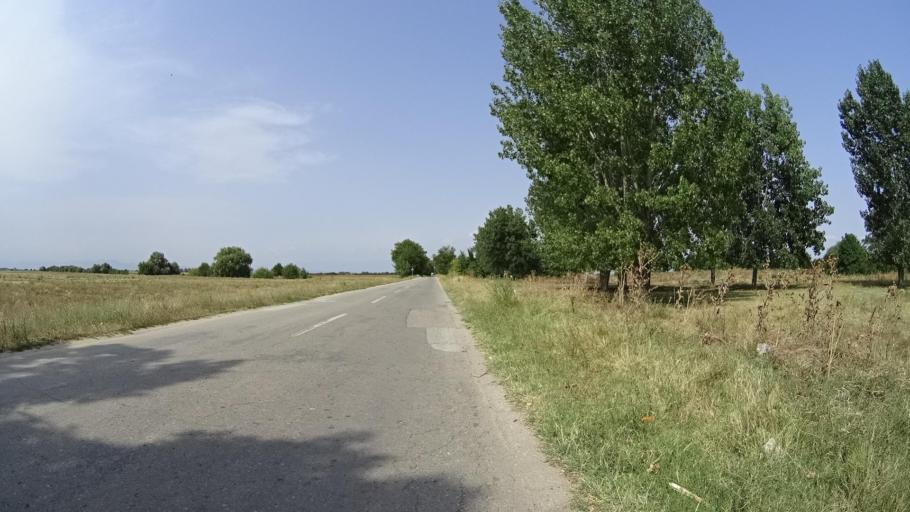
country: BG
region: Plovdiv
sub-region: Obshtina Plovdiv
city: Plovdiv
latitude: 42.2483
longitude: 24.7966
